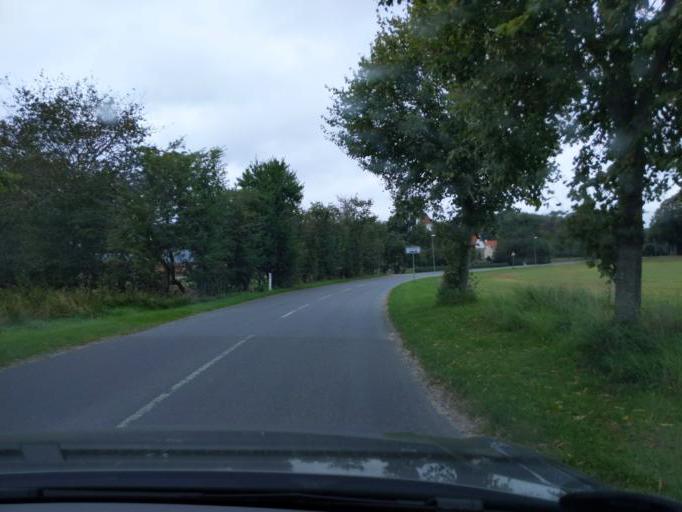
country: DK
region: North Denmark
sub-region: Mariagerfjord Kommune
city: Hobro
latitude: 56.5600
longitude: 9.6872
